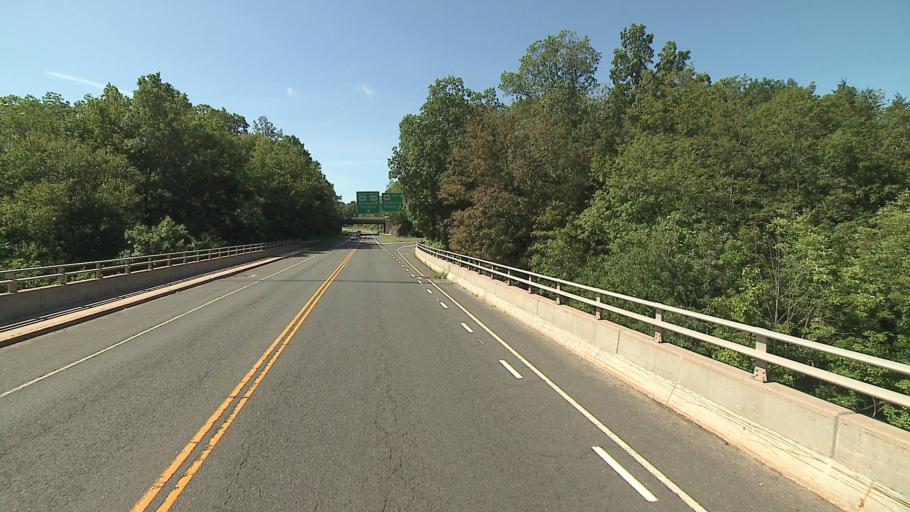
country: US
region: Connecticut
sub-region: Hartford County
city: Tariffville
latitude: 41.8969
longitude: -72.7494
